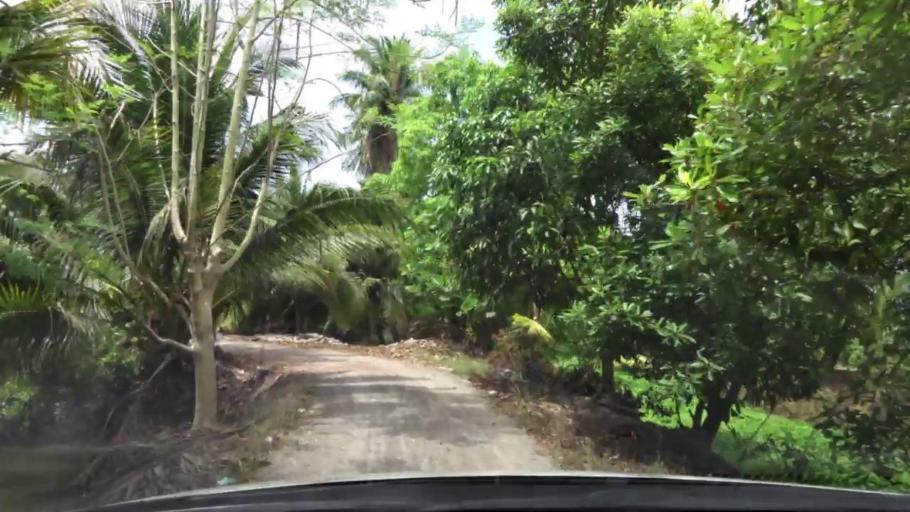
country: TH
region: Ratchaburi
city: Damnoen Saduak
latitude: 13.5168
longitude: 100.0150
